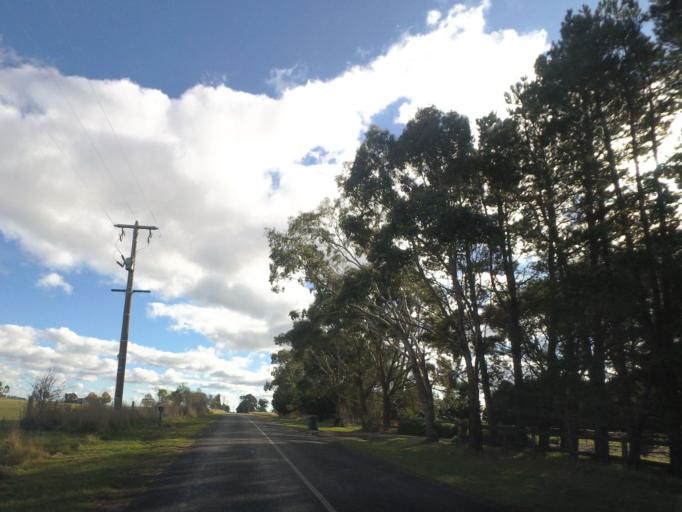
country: AU
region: Victoria
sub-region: Mount Alexander
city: Castlemaine
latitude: -37.2517
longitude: 144.4052
